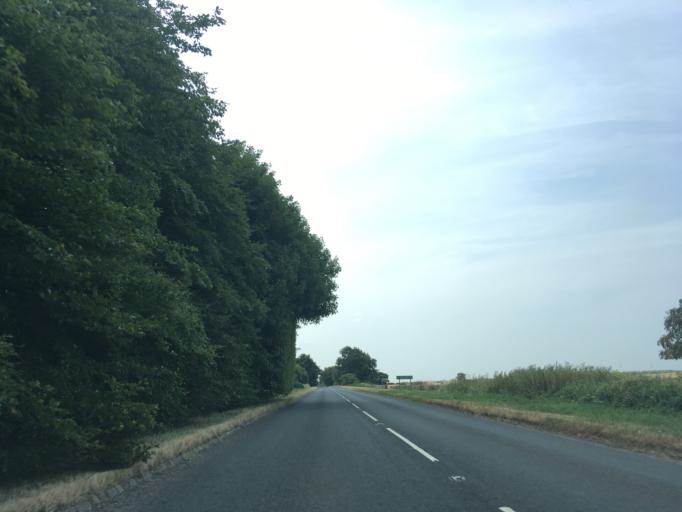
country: GB
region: England
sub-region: Gloucestershire
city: Nailsworth
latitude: 51.6623
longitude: -2.2319
